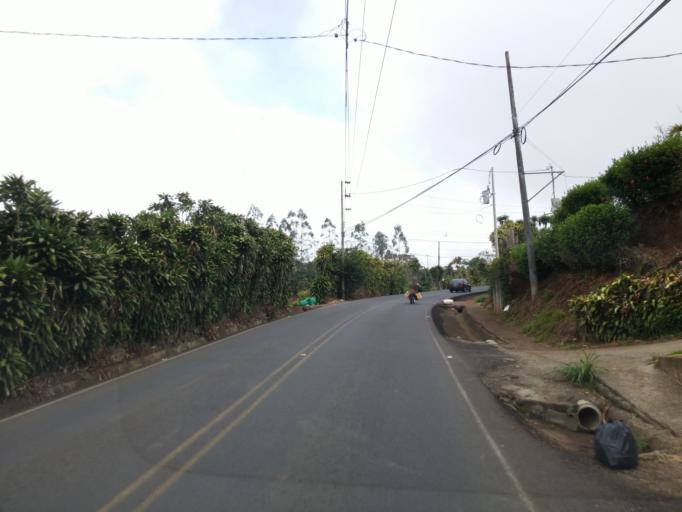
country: CR
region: Alajuela
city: San Ramon
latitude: 10.1249
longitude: -84.4723
